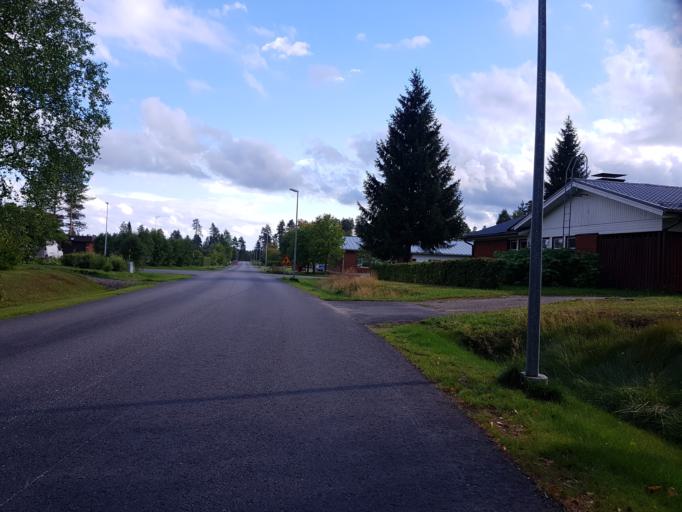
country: FI
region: Kainuu
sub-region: Kehys-Kainuu
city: Kuhmo
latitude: 64.1212
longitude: 29.5345
